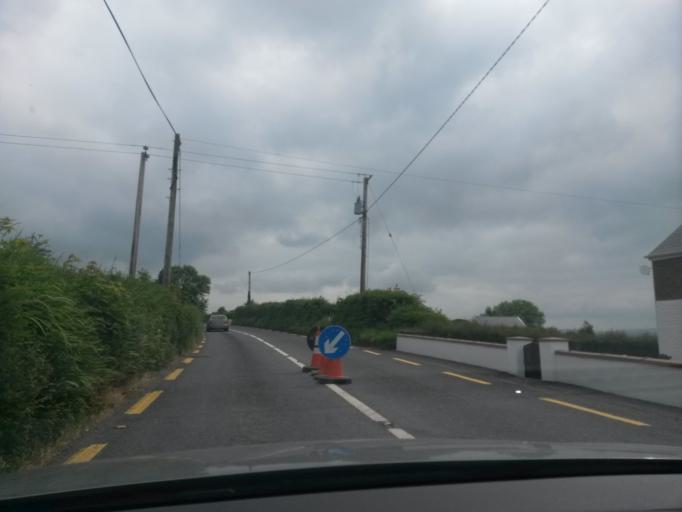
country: IE
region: Munster
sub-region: Ciarrai
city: Tralee
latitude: 52.1932
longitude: -9.6833
